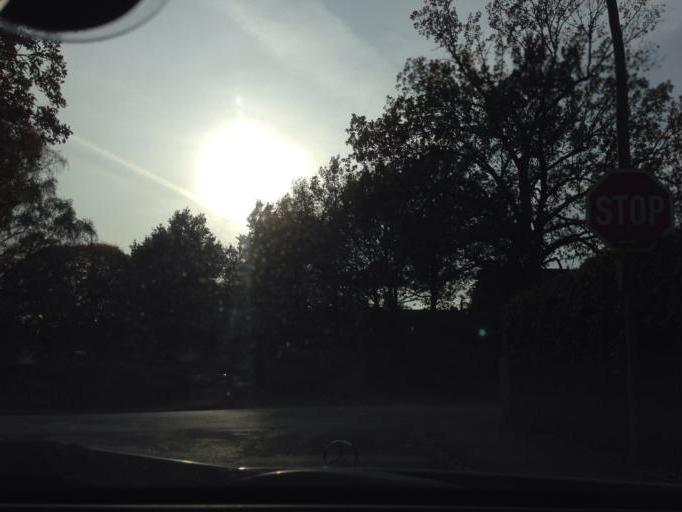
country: DE
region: Schleswig-Holstein
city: Barsbuettel
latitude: 53.5946
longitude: 10.1750
